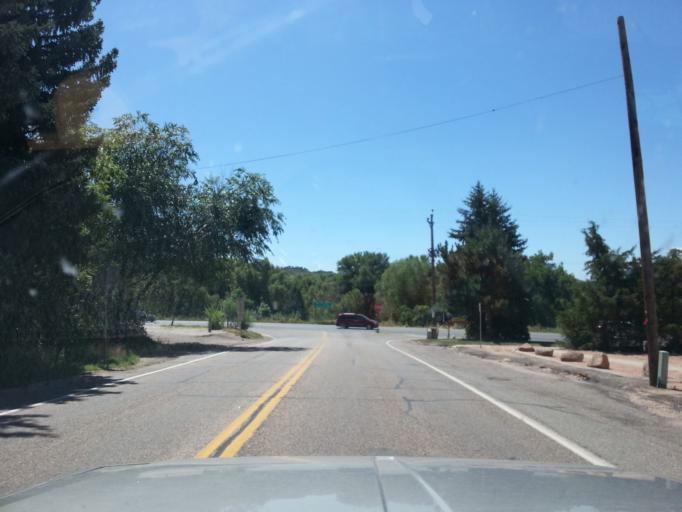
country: US
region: Colorado
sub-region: Larimer County
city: Loveland
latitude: 40.4187
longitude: -105.1887
